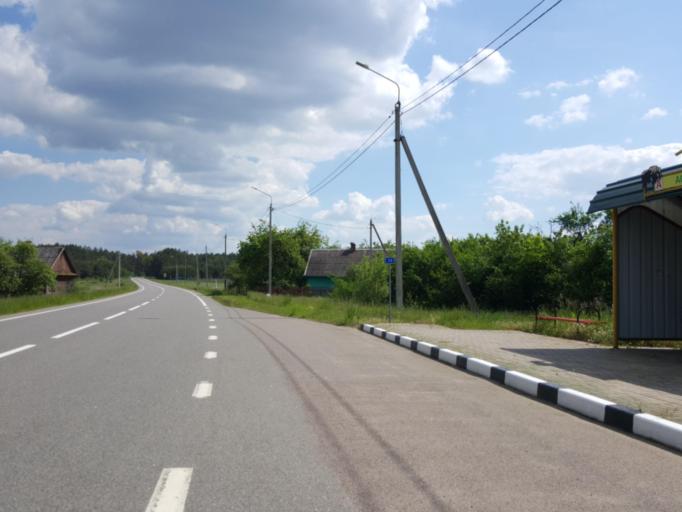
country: BY
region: Brest
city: Kamyanyuki
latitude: 52.5250
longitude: 23.6563
